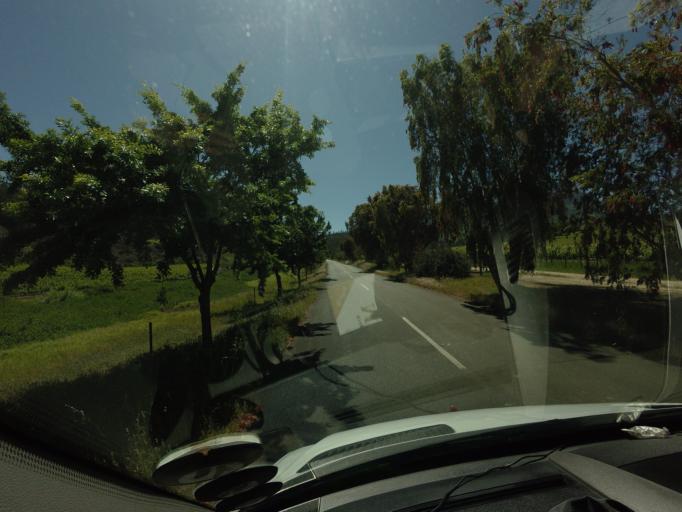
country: ZA
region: Western Cape
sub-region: Cape Winelands District Municipality
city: Stellenbosch
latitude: -33.8716
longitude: 18.8652
